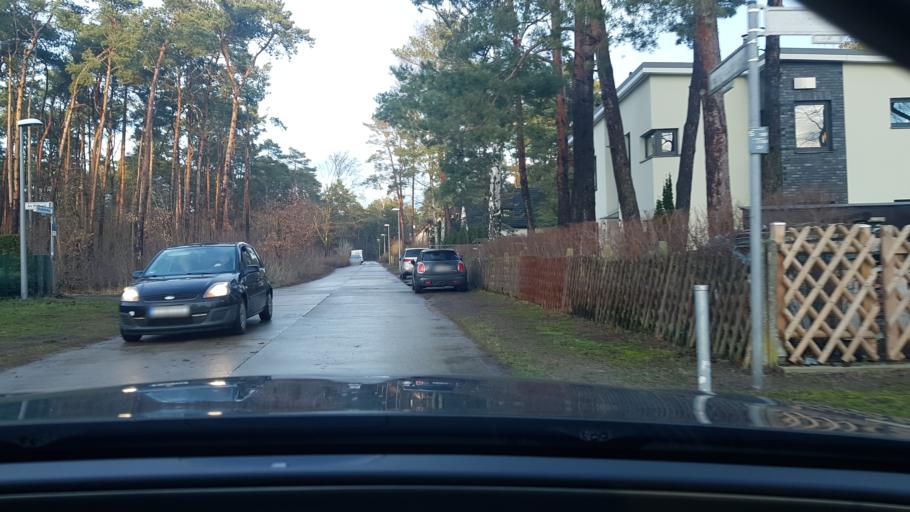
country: DE
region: Berlin
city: Muggelheim
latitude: 52.4217
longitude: 13.6702
